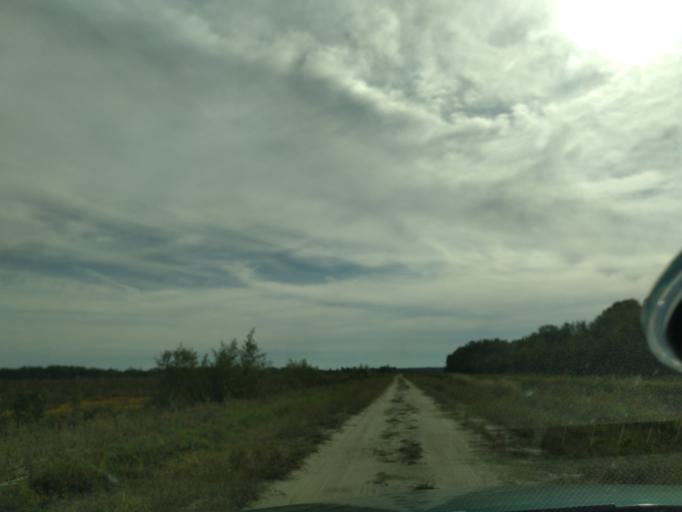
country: US
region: North Carolina
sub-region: Beaufort County
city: Belhaven
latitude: 35.7161
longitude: -76.5772
